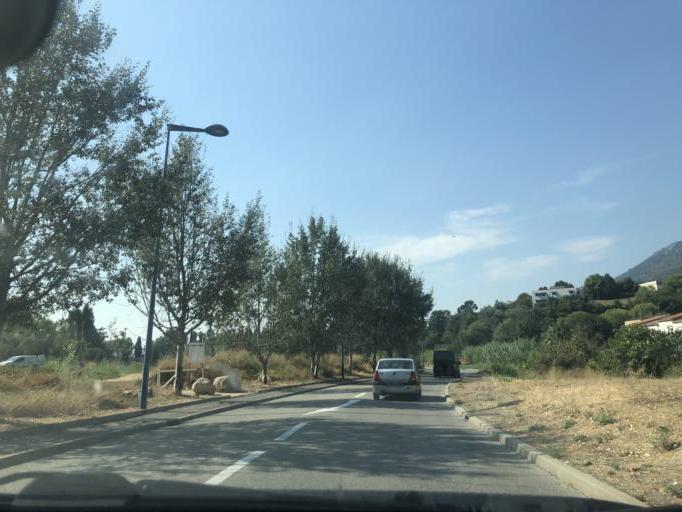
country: FR
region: Provence-Alpes-Cote d'Azur
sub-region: Departement des Alpes-Maritimes
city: Colomars
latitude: 43.7697
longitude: 7.2023
